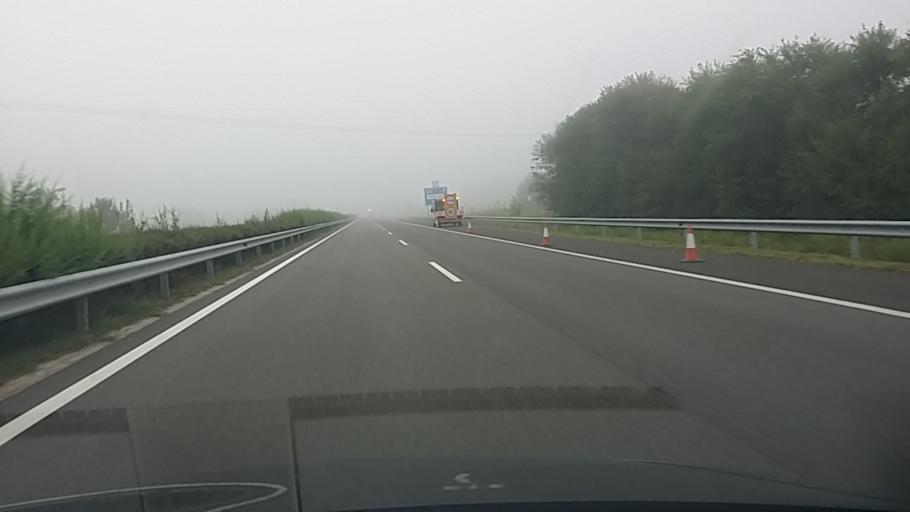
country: HU
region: Csongrad
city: Domaszek
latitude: 46.2586
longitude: 20.0383
